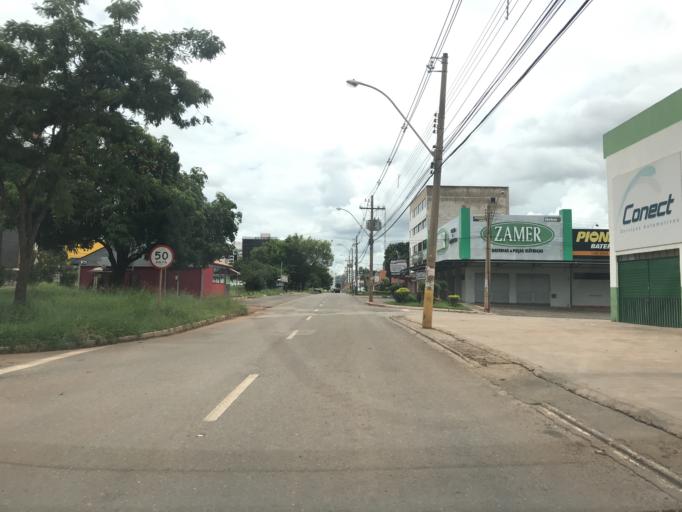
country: BR
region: Federal District
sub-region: Brasilia
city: Brasilia
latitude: -15.8232
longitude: -47.9564
